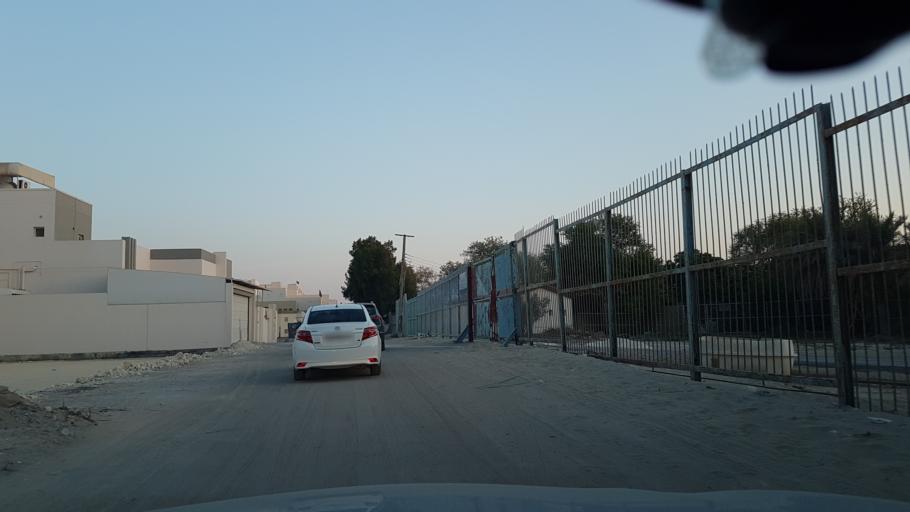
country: BH
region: Manama
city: Jidd Hafs
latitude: 26.2352
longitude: 50.5056
